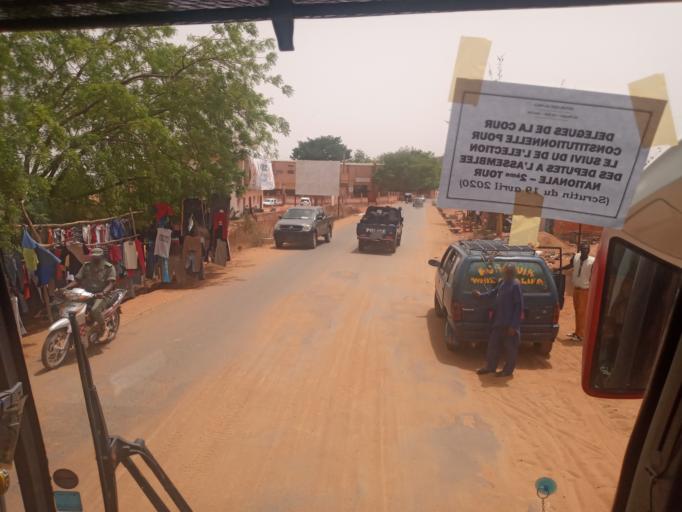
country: ML
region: Koulikoro
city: Koulikoro
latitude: 12.8768
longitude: -7.5479
